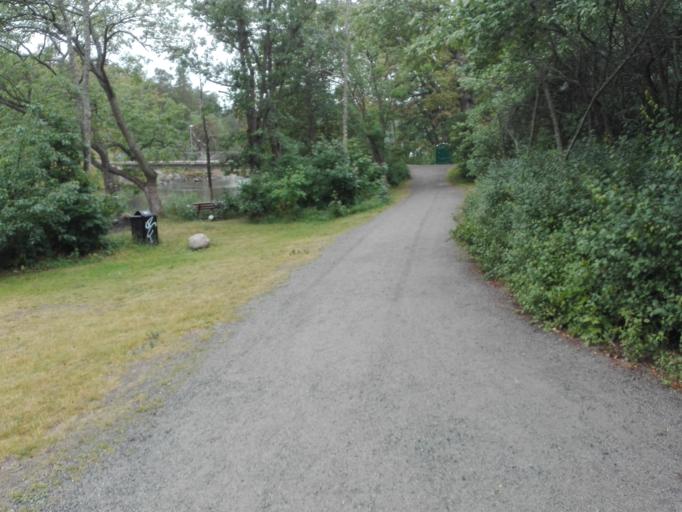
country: SE
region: Stockholm
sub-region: Nacka Kommun
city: Fisksatra
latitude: 59.2967
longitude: 18.2576
